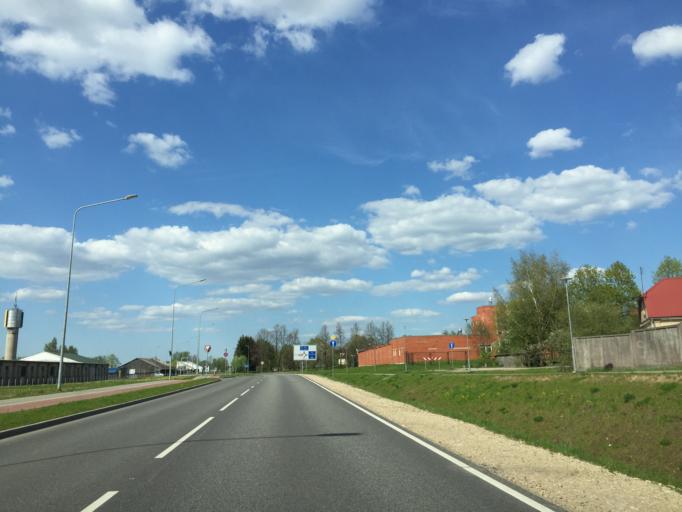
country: LV
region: Limbazu Rajons
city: Limbazi
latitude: 57.5108
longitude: 24.7237
